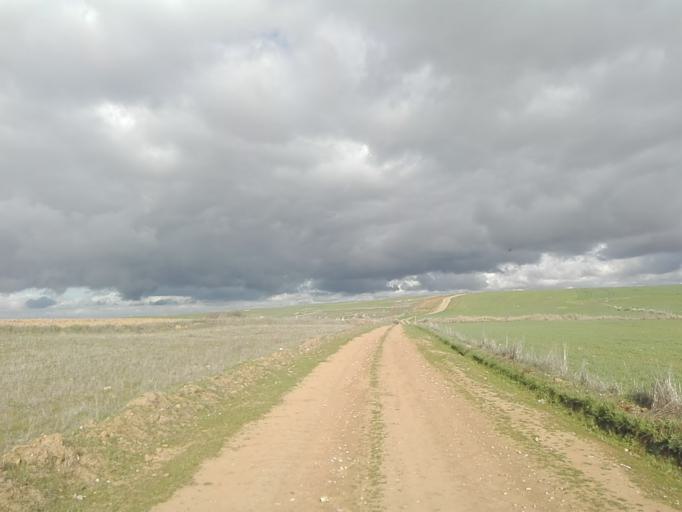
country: ES
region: Extremadura
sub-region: Provincia de Badajoz
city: Llerena
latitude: 38.2793
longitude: -6.0240
